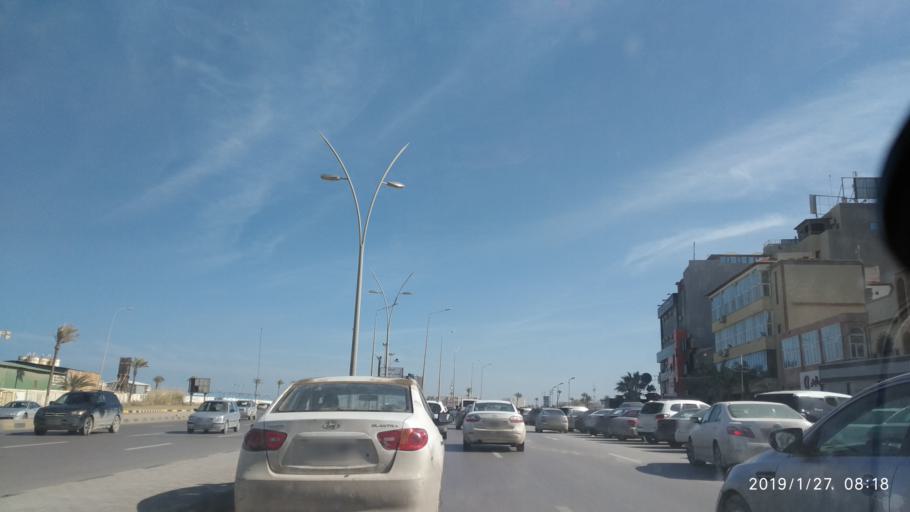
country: LY
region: Tripoli
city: Tripoli
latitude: 32.9067
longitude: 13.2649
